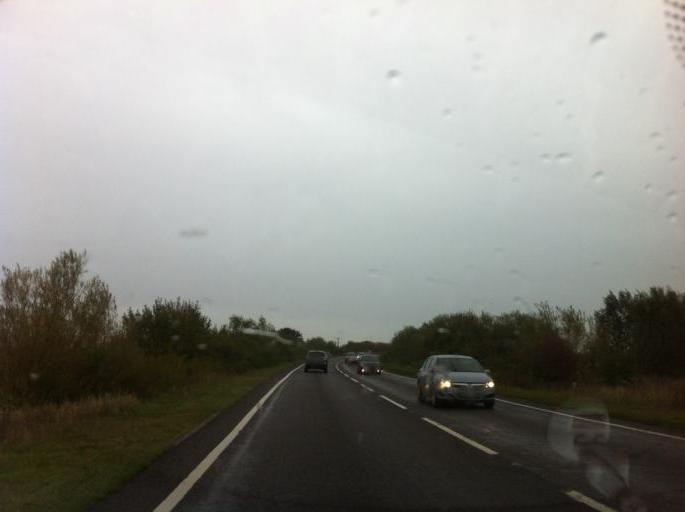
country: GB
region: England
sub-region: Peterborough
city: Newborough
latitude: 52.6278
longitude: -0.2045
